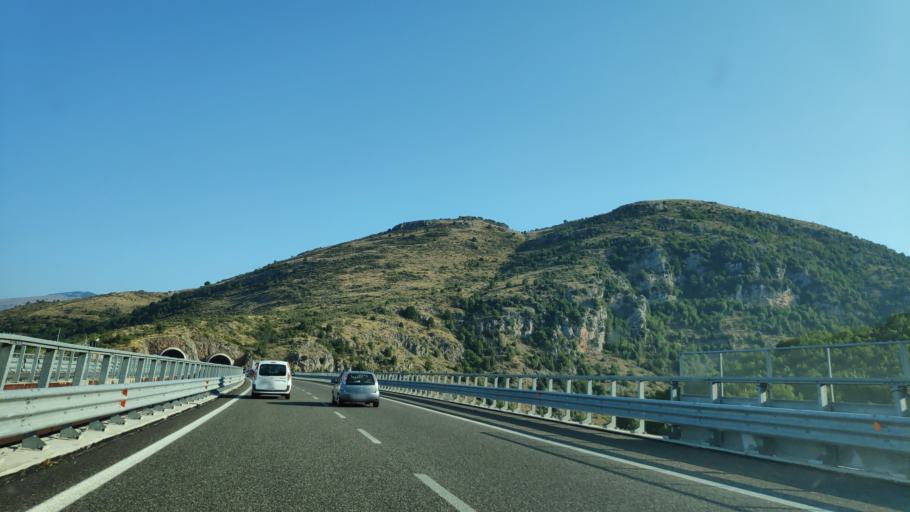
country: IT
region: Basilicate
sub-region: Provincia di Potenza
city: Lauria
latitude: 40.0342
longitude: 15.8743
